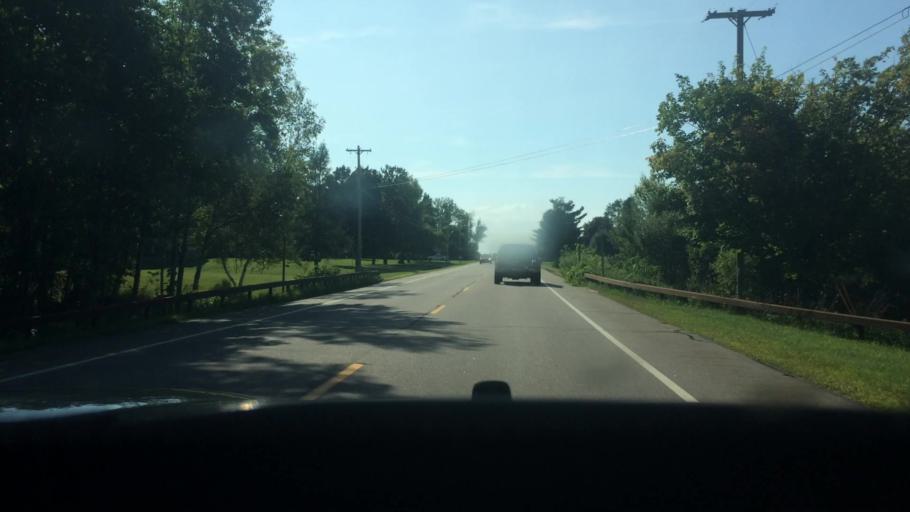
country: US
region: New York
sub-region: Franklin County
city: Malone
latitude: 44.8587
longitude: -74.2405
